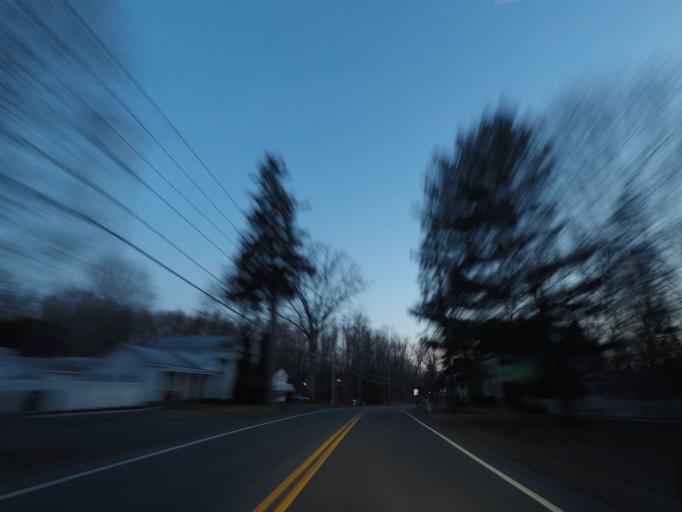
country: US
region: New York
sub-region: Schenectady County
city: Niskayuna
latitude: 42.8000
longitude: -73.8267
